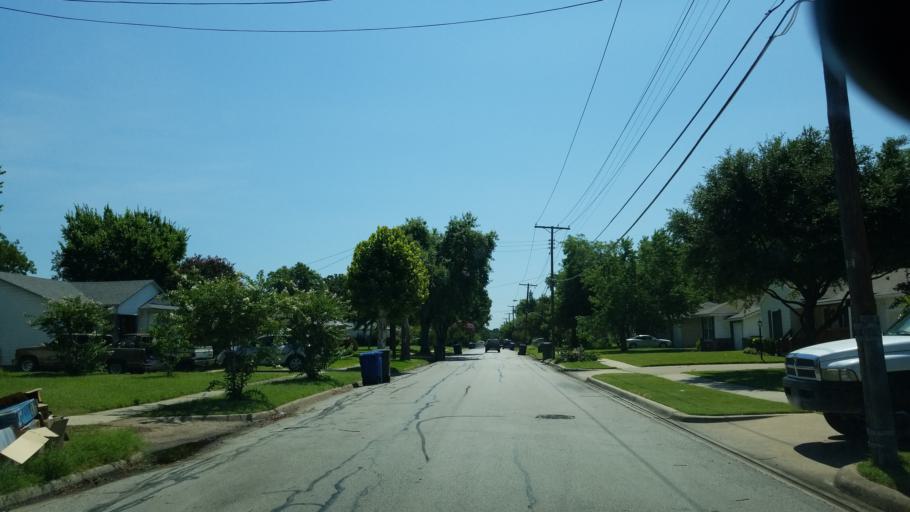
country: US
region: Texas
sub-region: Dallas County
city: Carrollton
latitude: 32.9649
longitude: -96.9058
